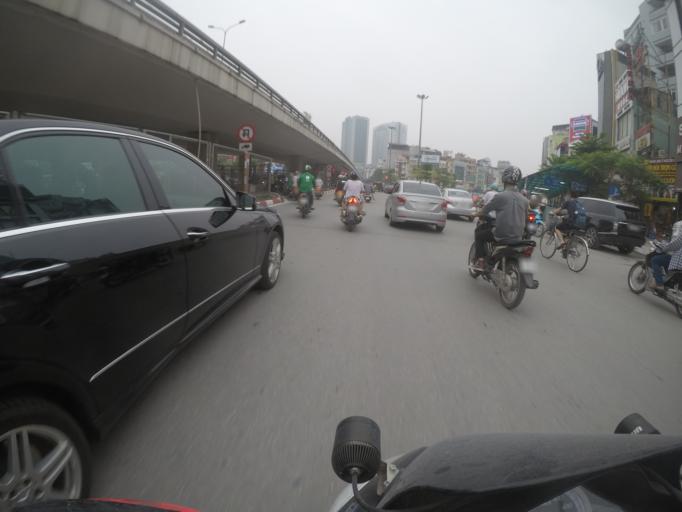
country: VN
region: Ha Noi
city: Dong Da
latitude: 21.0025
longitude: 105.8196
